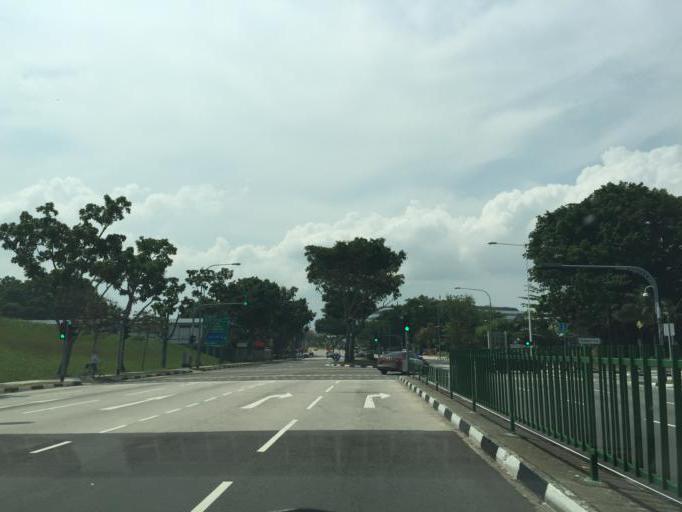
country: SG
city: Singapore
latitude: 1.3370
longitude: 103.9593
